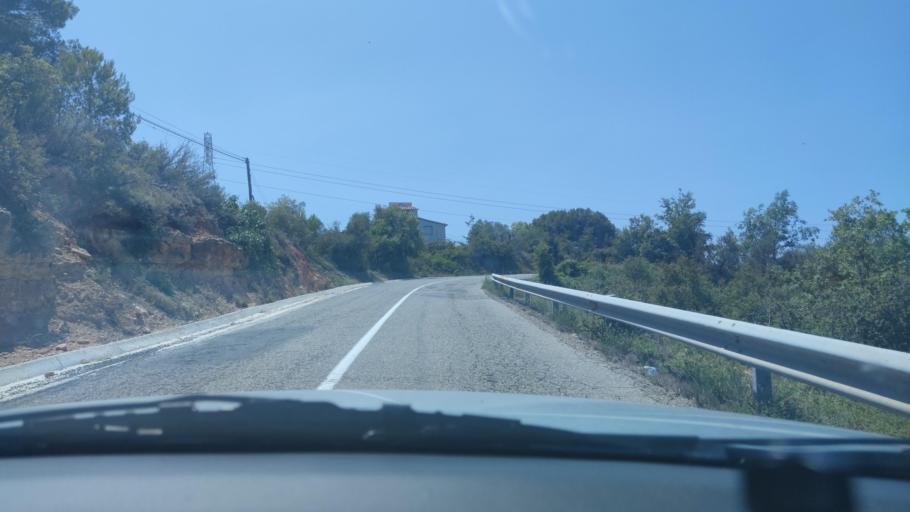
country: ES
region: Catalonia
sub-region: Provincia de Tarragona
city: Vallclara
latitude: 41.3934
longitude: 0.9514
